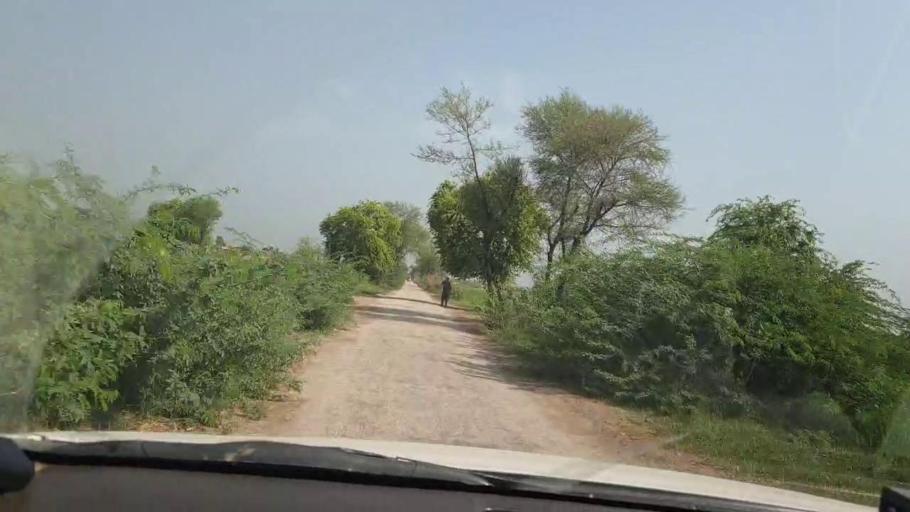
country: PK
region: Sindh
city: Chak
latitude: 27.8332
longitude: 68.7992
